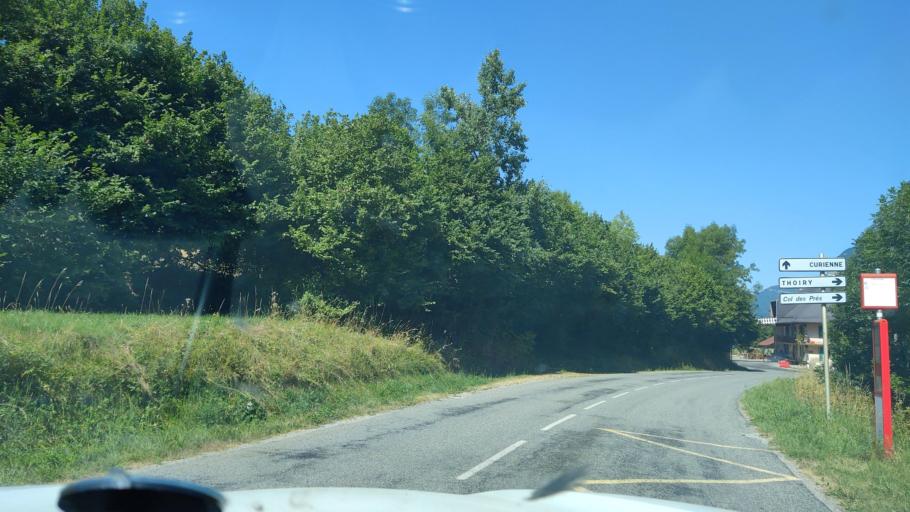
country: FR
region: Rhone-Alpes
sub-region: Departement de la Savoie
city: Barby
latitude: 45.5722
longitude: 6.0323
